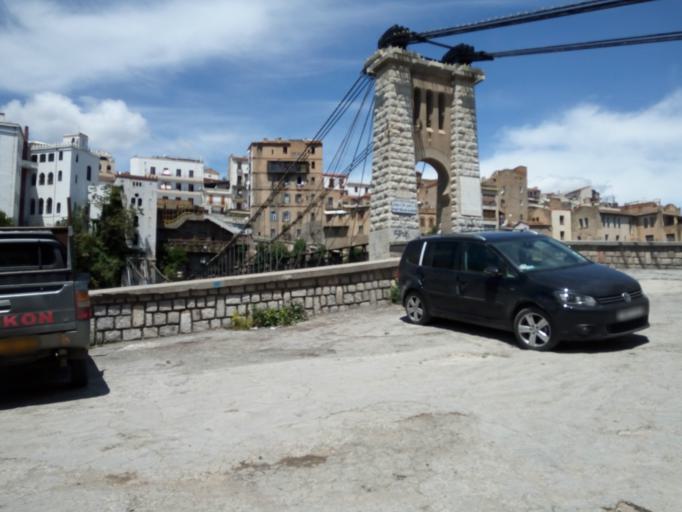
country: DZ
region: Constantine
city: Constantine
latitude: 36.3658
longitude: 6.6156
